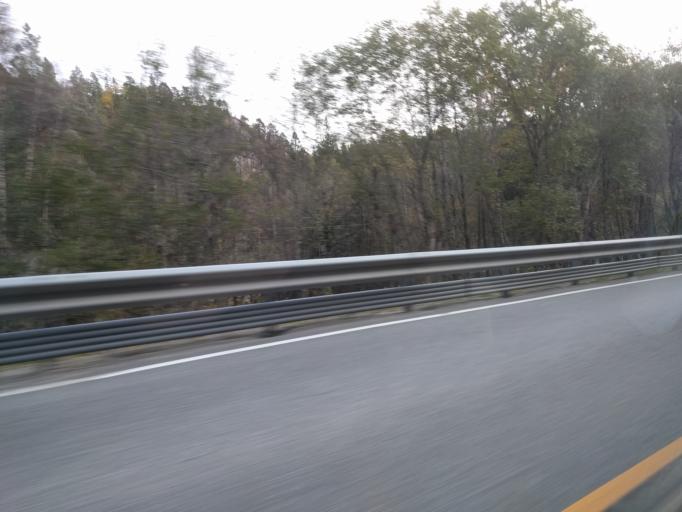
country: NO
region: Vest-Agder
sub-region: Kristiansand
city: Strai
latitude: 58.2530
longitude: 7.8609
